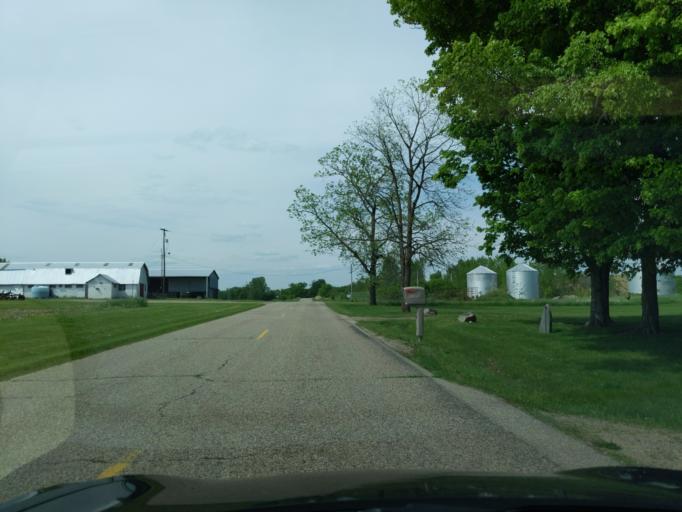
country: US
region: Michigan
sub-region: Ingham County
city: Leslie
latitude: 42.4186
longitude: -84.3335
